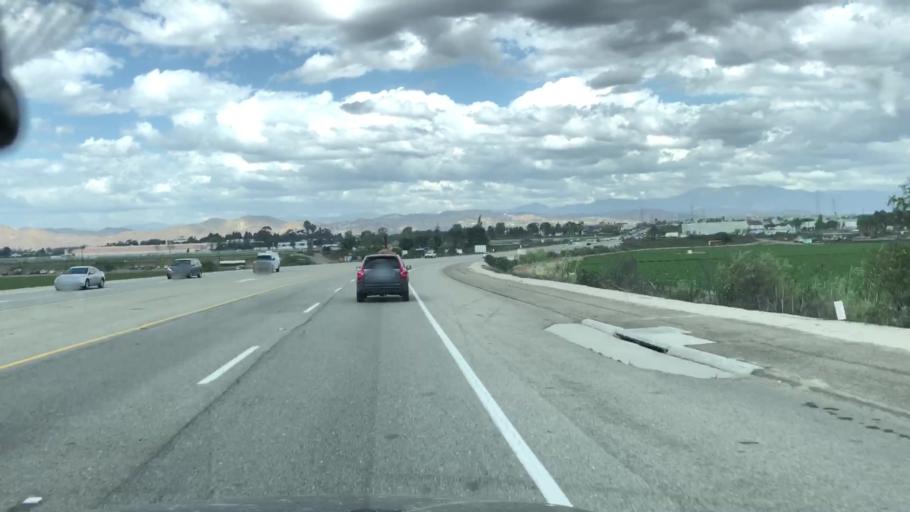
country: US
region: California
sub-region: Ventura County
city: El Rio
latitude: 34.2393
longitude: -119.2164
